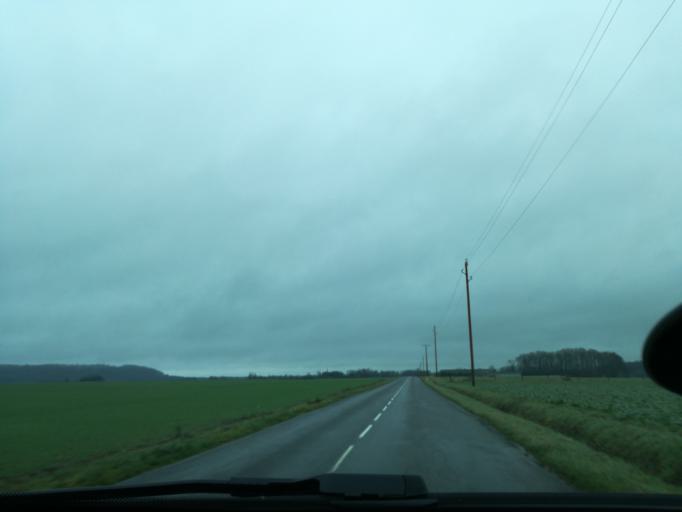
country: FR
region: Lorraine
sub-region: Departement de la Meuse
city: Clermont-en-Argonne
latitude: 49.0037
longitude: 5.0993
